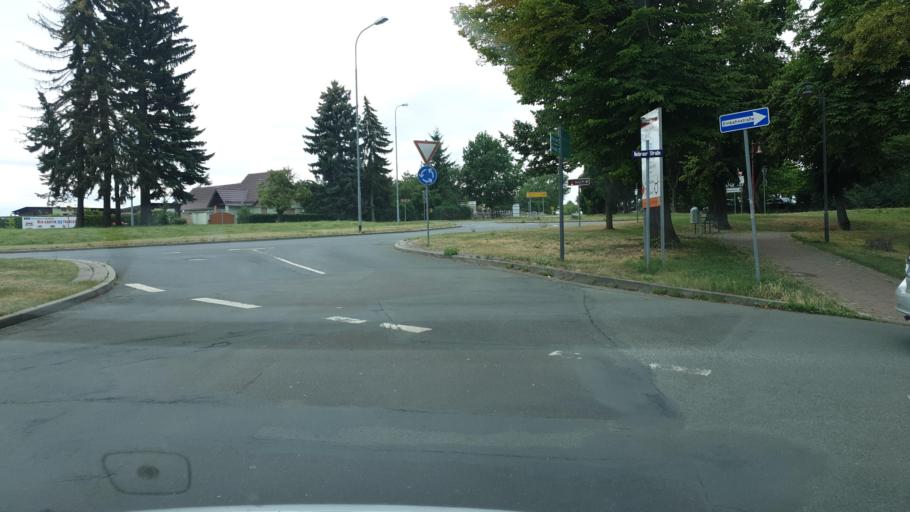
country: DE
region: Saxony-Anhalt
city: Querfurt
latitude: 51.3754
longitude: 11.5991
